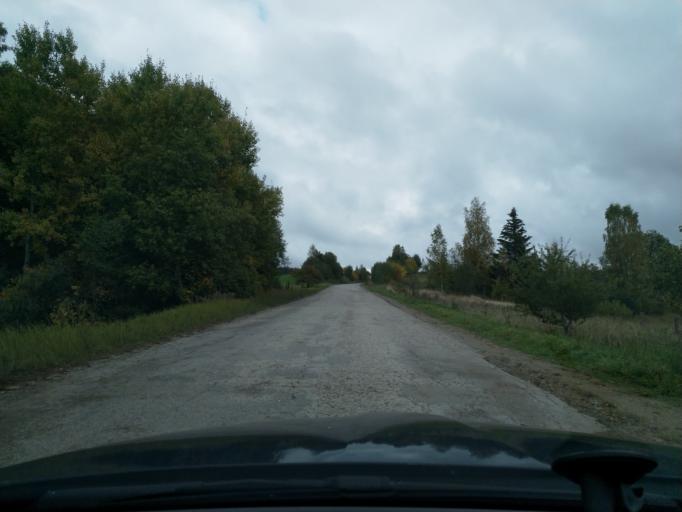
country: LV
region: Alsunga
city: Alsunga
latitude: 57.0247
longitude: 21.6808
